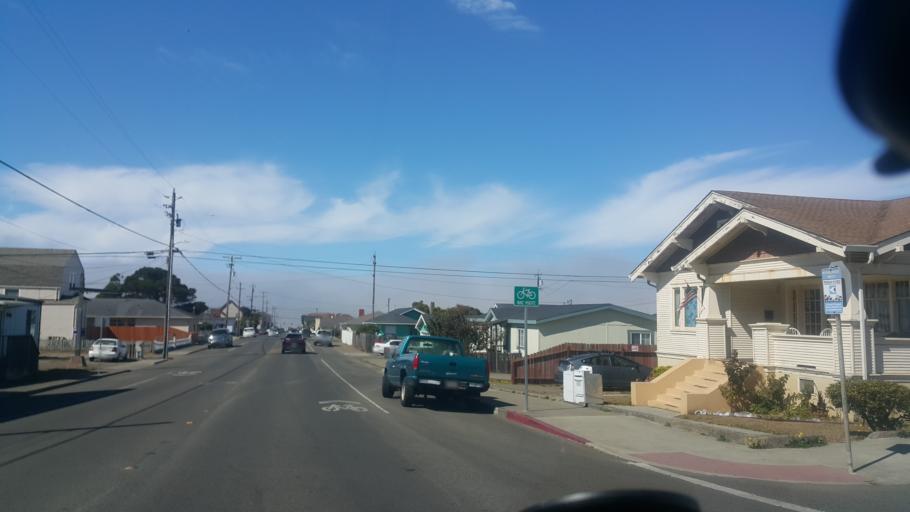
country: US
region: California
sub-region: Mendocino County
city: Fort Bragg
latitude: 39.4417
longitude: -123.7994
